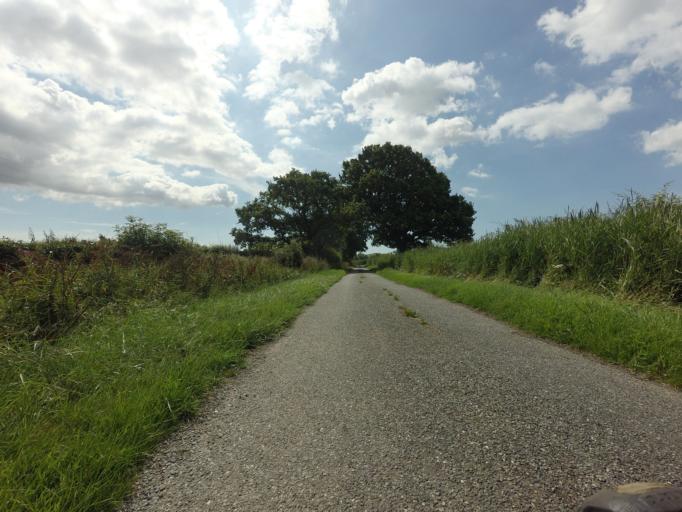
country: GB
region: England
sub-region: Kent
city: Stone
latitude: 51.0500
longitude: 0.7722
